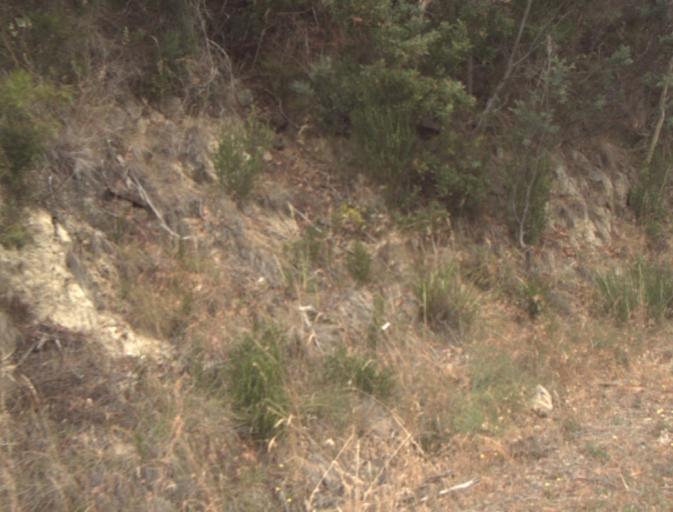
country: AU
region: Tasmania
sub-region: Northern Midlands
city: Evandale
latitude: -41.4941
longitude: 147.4250
